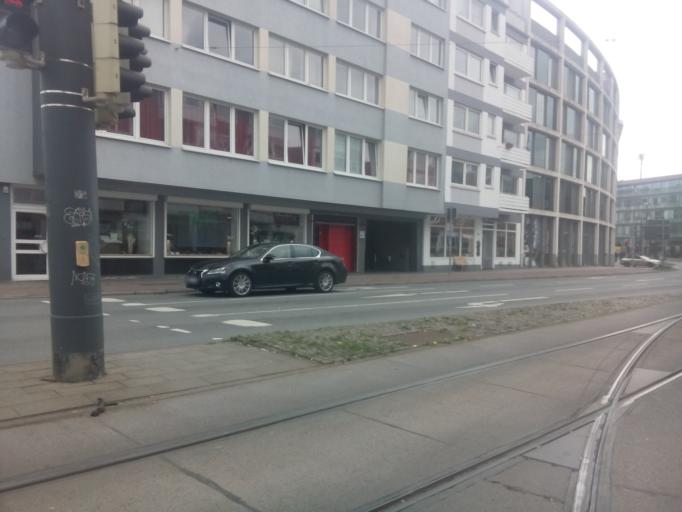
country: DE
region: Bremen
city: Bremen
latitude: 53.0818
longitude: 8.7963
